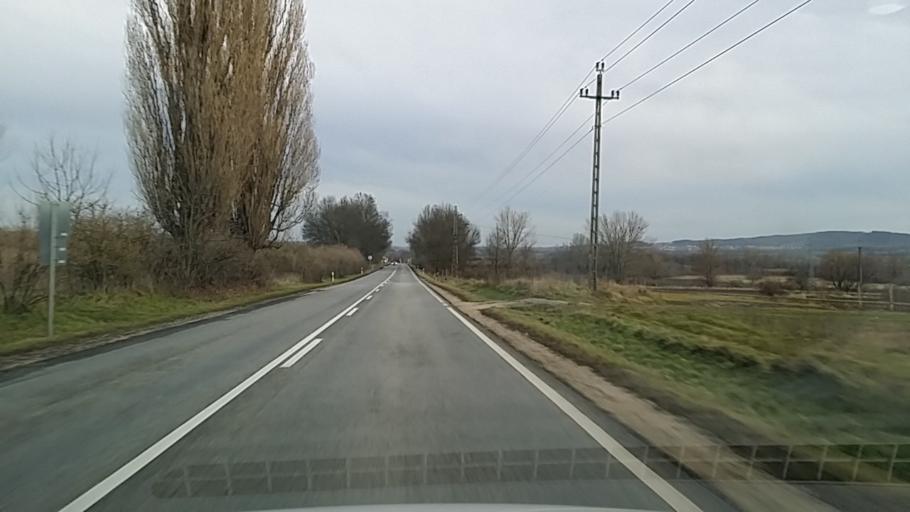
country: HU
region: Fejer
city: Mor
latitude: 47.3610
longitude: 18.2057
